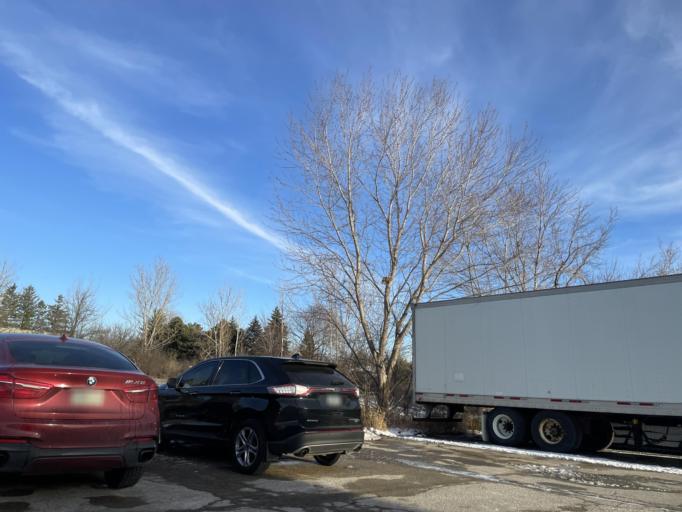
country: CA
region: Ontario
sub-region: Wellington County
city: Guelph
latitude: 43.5458
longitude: -80.2835
